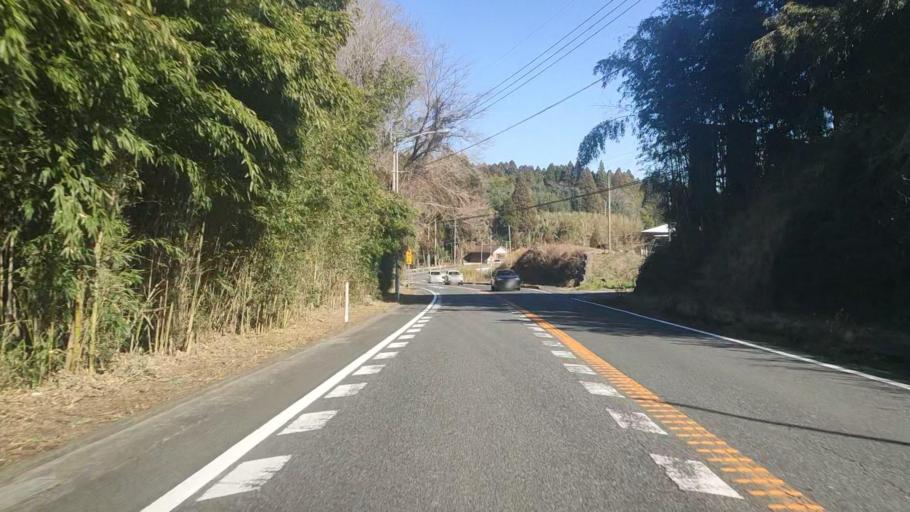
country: JP
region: Kagoshima
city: Sueyoshicho-ninokata
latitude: 31.6926
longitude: 130.9726
